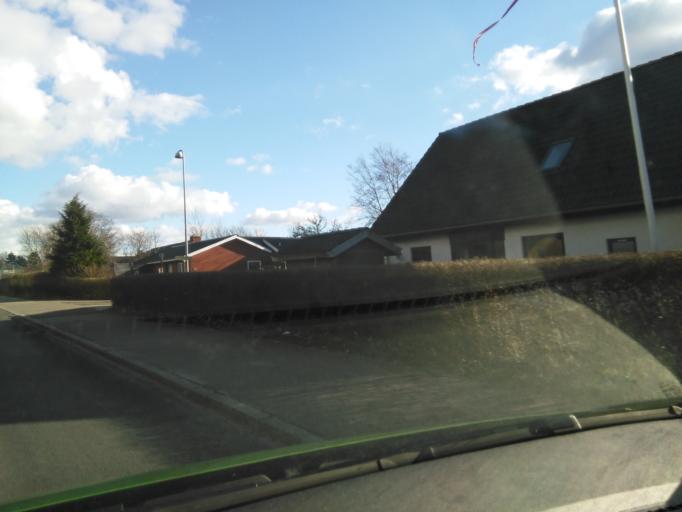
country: DK
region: Central Jutland
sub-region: Silkeborg Kommune
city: Silkeborg
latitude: 56.1837
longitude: 9.5160
